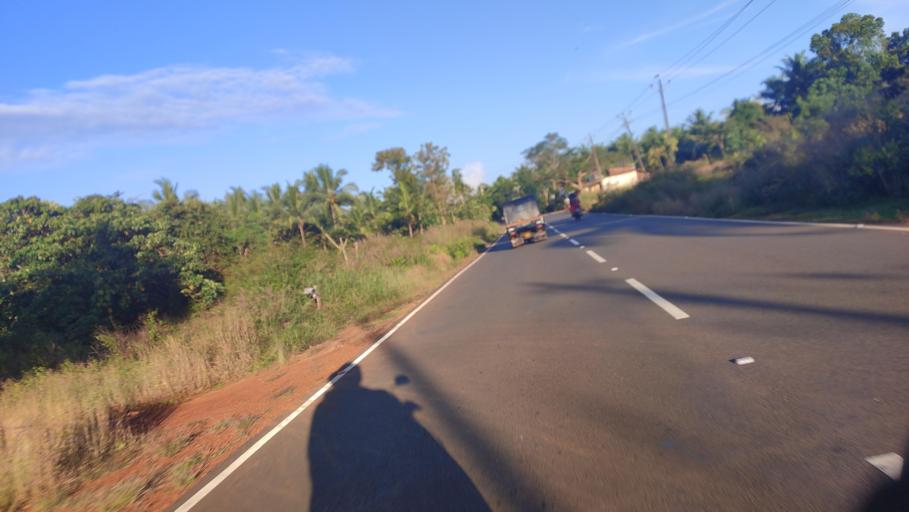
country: IN
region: Kerala
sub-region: Kasaragod District
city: Kasaragod
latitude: 12.4650
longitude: 75.0747
